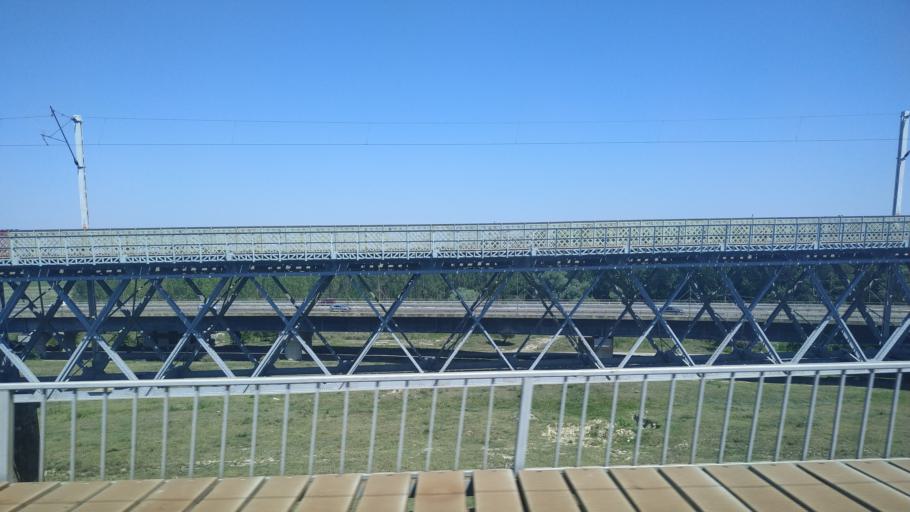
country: RO
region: Constanta
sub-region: Oras Cernavoda
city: Cernavoda
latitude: 44.3436
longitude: 28.0027
